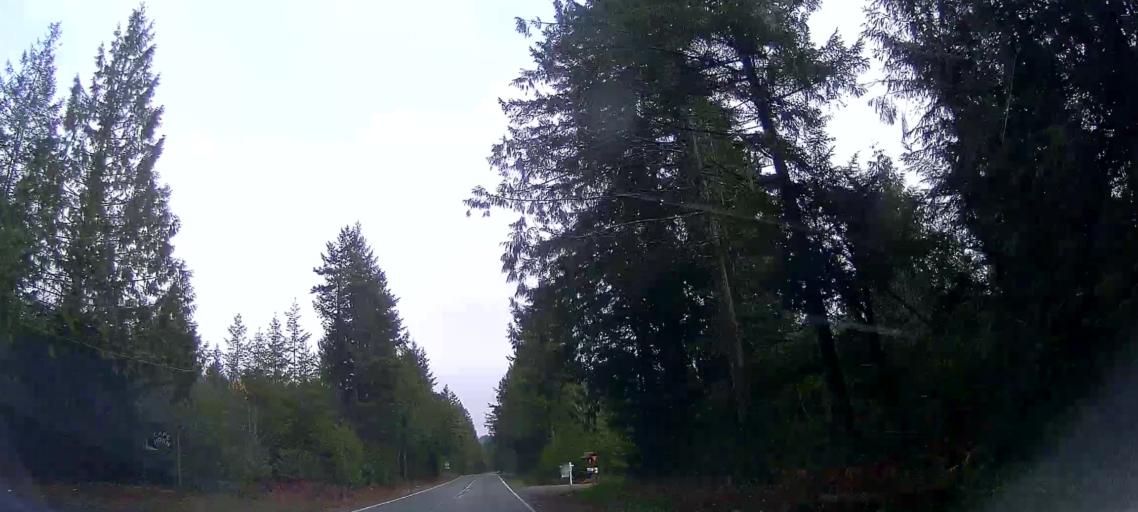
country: US
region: Washington
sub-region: Snohomish County
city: Darrington
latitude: 48.5280
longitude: -121.8259
